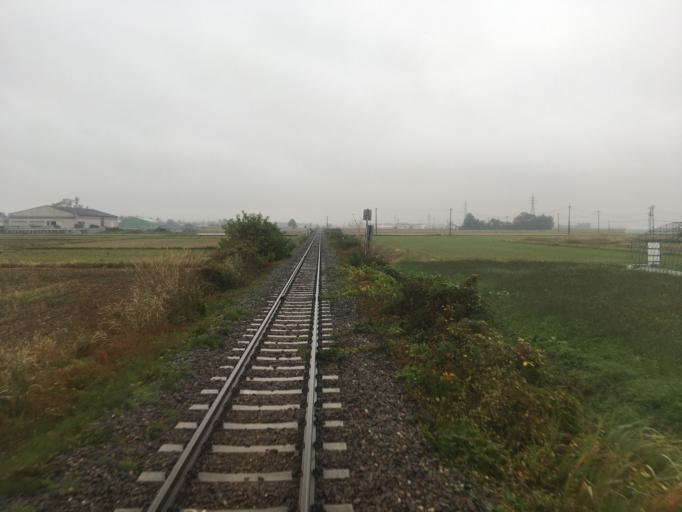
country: JP
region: Miyagi
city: Furukawa
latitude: 38.5646
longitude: 141.0021
